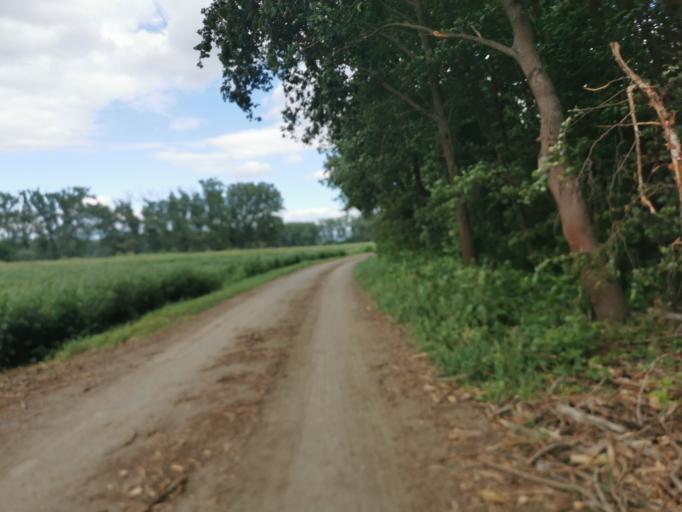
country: CZ
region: South Moravian
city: Straznice
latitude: 48.9349
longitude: 17.3068
